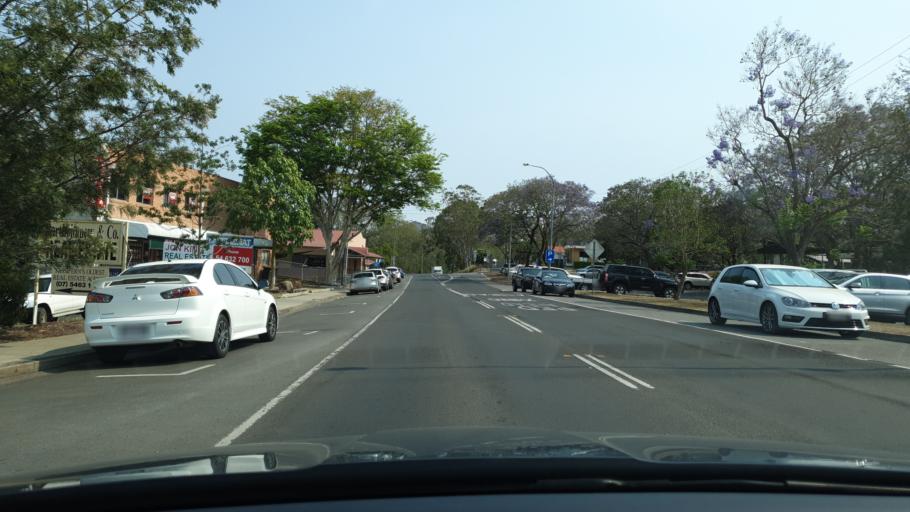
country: AU
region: Queensland
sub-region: Ipswich
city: Deebing Heights
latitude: -27.9975
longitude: 152.6815
